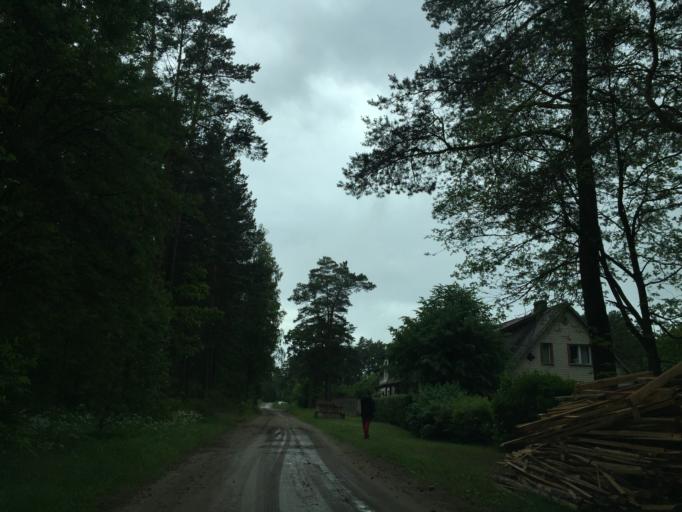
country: LV
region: Riga
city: Jaunciems
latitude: 57.0539
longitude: 24.1752
